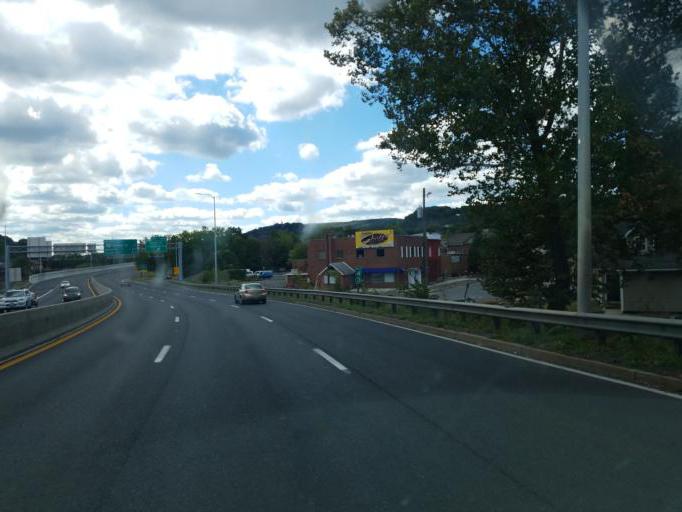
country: US
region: Maryland
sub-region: Allegany County
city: Cumberland
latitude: 39.6492
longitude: -78.7681
